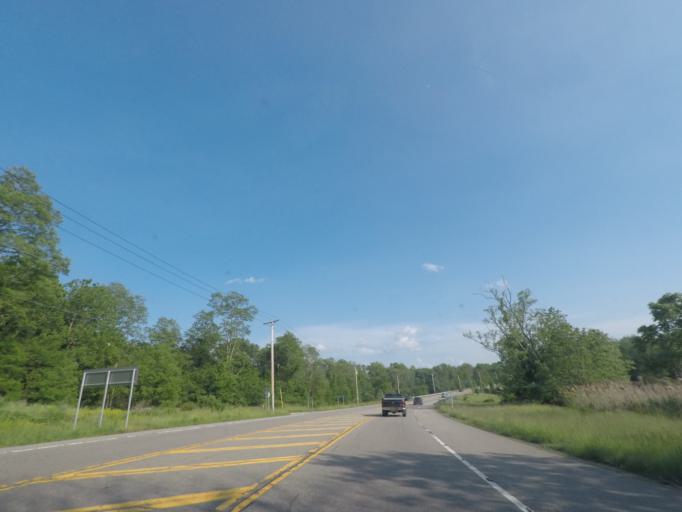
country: US
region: New York
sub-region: Orange County
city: Beaverdam Lake-Salisbury Mills
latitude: 41.4951
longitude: -74.1325
